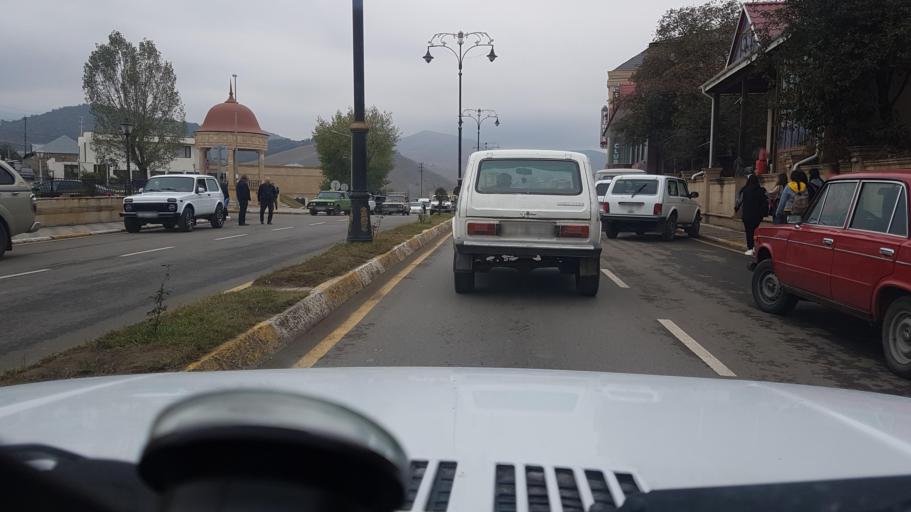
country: AZ
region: Gadabay Rayon
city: Kyadabek
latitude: 40.5757
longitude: 45.8082
